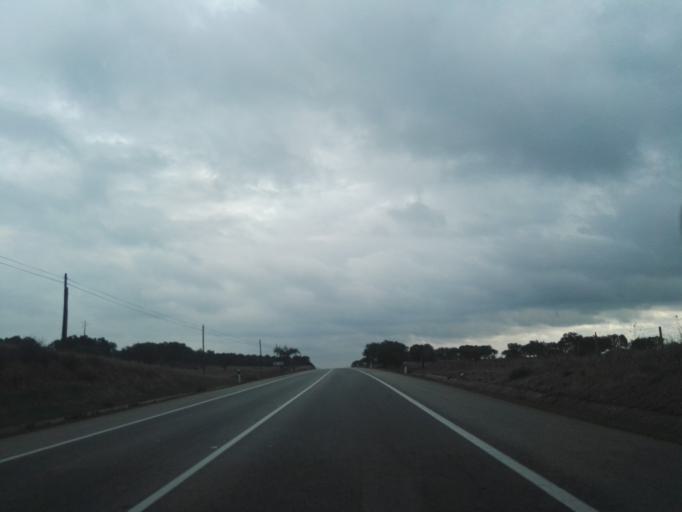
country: PT
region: Portalegre
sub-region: Arronches
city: Arronches
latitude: 39.1513
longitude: -7.3113
